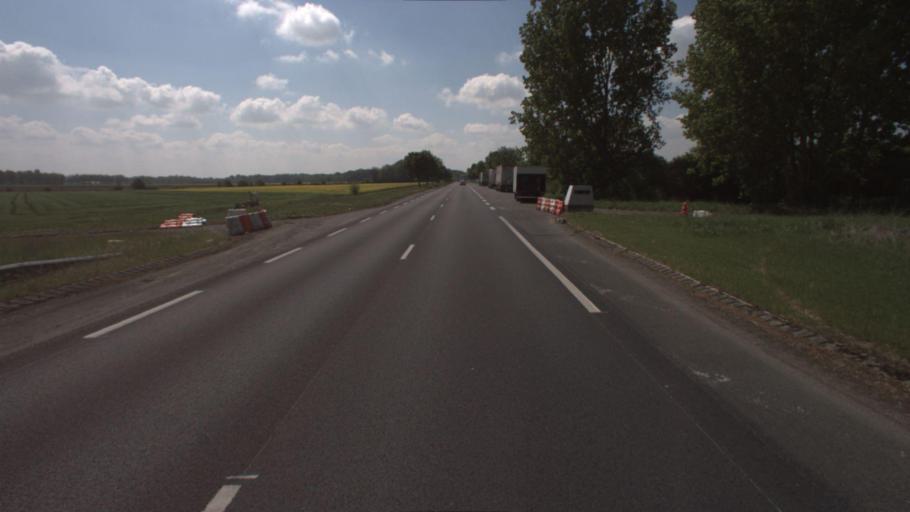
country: FR
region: Ile-de-France
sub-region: Departement de Seine-et-Marne
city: La Houssaye-en-Brie
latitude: 48.7487
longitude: 2.8580
